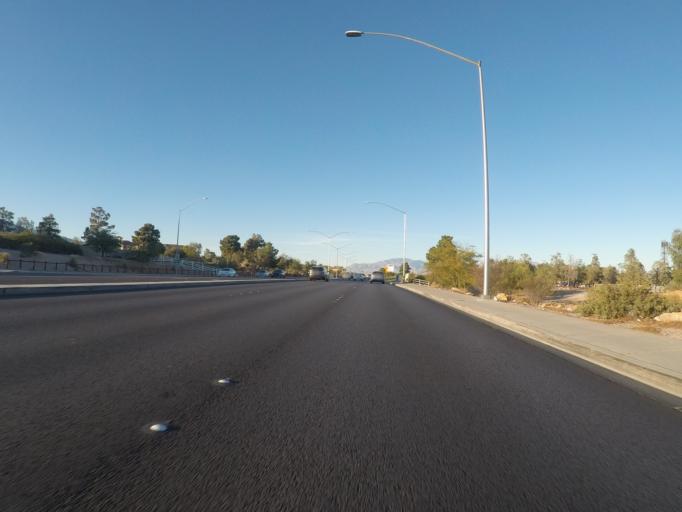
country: US
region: Nevada
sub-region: Clark County
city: Summerlin South
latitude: 36.1703
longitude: -115.2869
